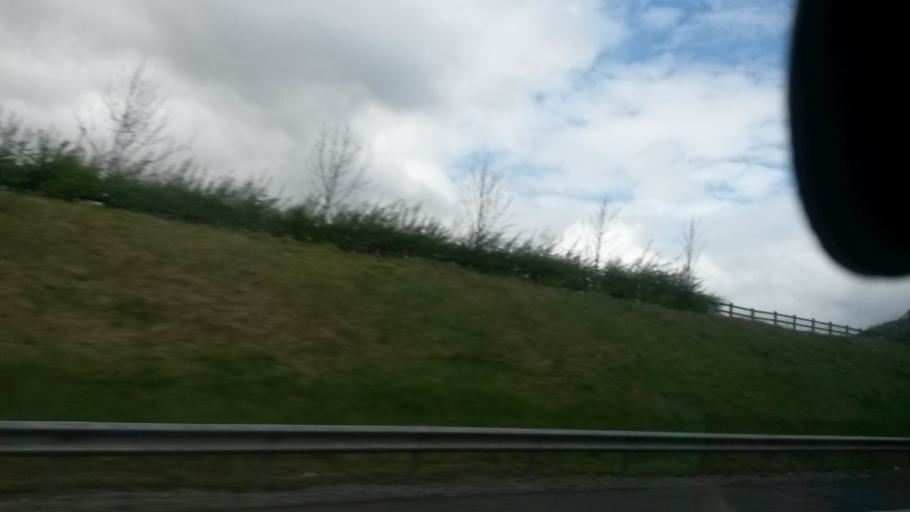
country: IE
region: Leinster
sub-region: Laois
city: Mountrath
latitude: 52.9015
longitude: -7.4891
